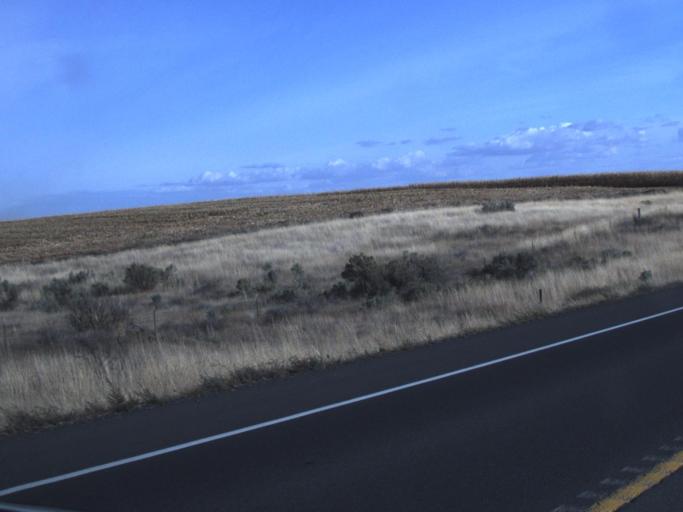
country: US
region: Oregon
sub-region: Umatilla County
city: Umatilla
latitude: 45.9534
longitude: -119.4048
